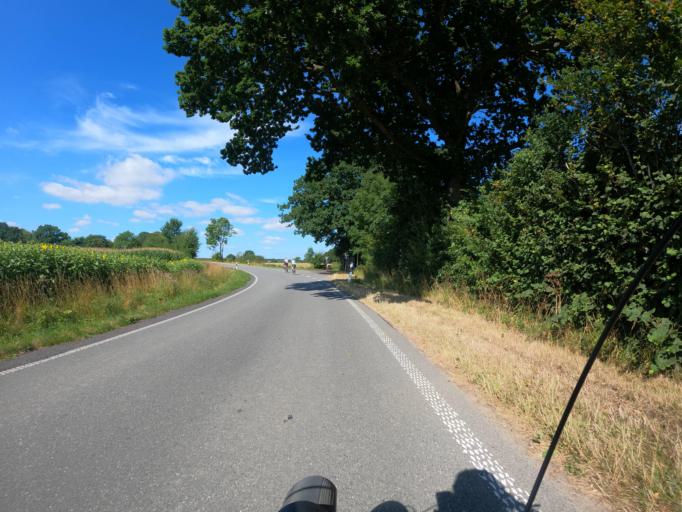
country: DE
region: Schleswig-Holstein
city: Steinbergkirche
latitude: 54.7974
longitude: 9.7451
